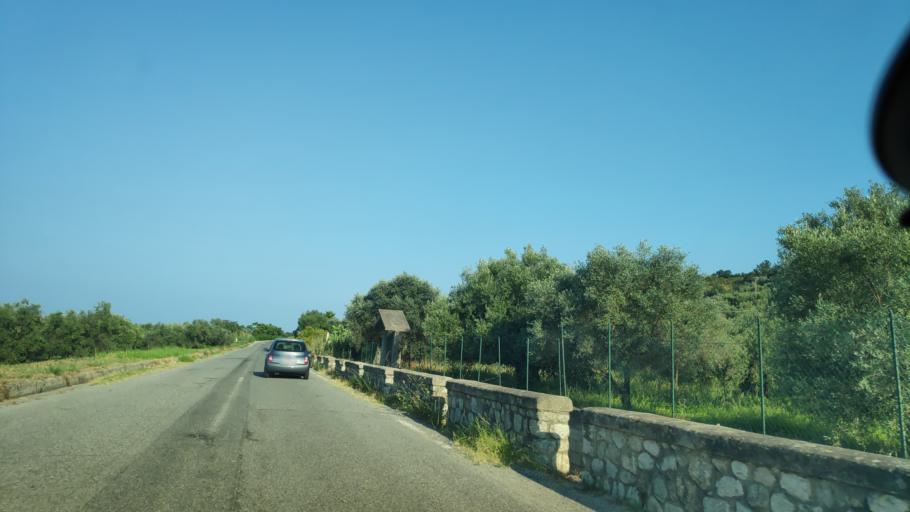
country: IT
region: Calabria
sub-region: Provincia di Reggio Calabria
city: Monasterace
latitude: 38.4515
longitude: 16.5654
